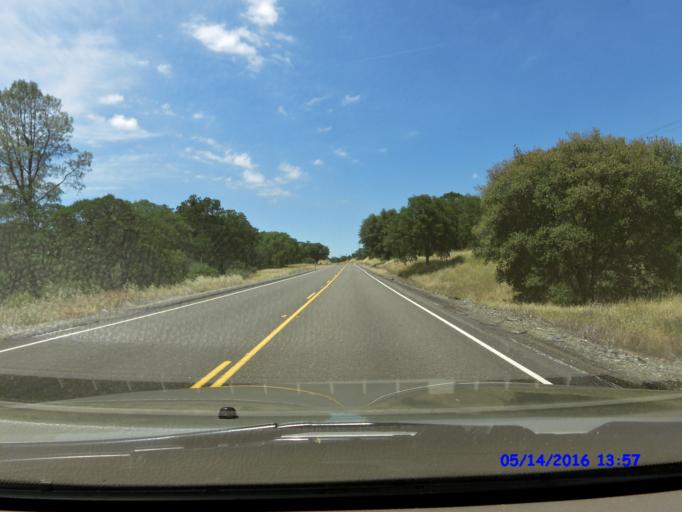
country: US
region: California
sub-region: Mariposa County
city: Mariposa
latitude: 37.5458
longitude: -120.0964
